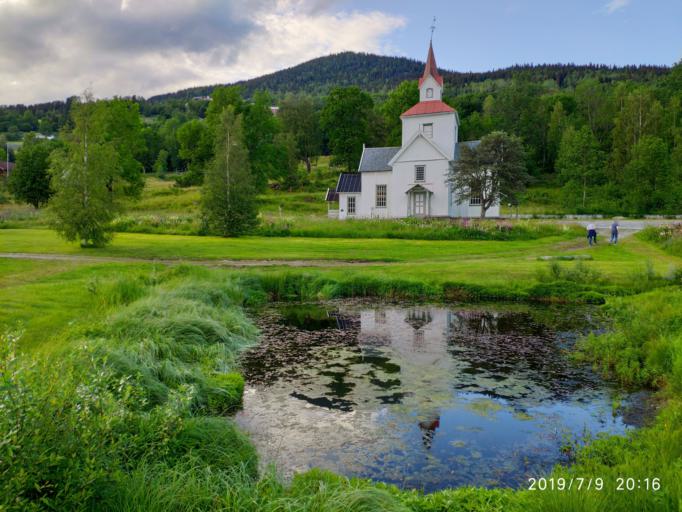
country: NO
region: Telemark
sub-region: Seljord
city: Seljord
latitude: 59.6035
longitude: 8.6393
